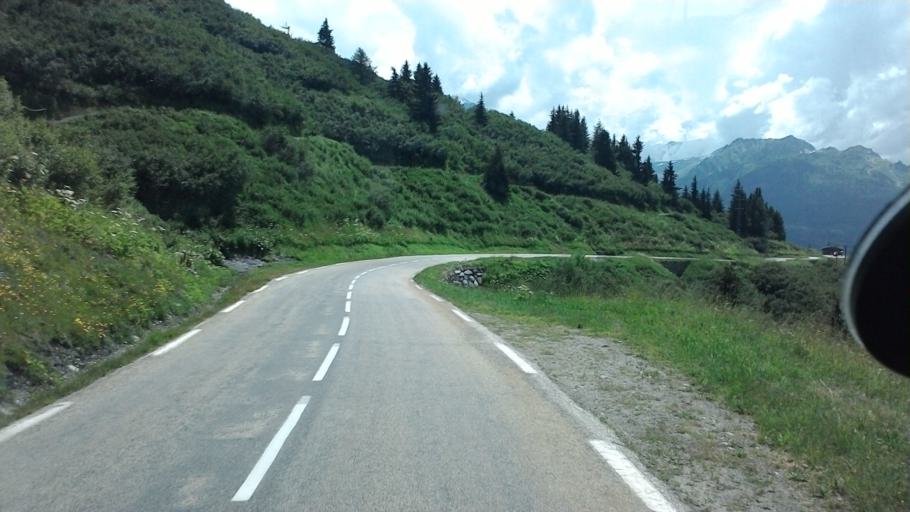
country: FR
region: Rhone-Alpes
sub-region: Departement de la Savoie
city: Seez
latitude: 45.6336
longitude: 6.8491
